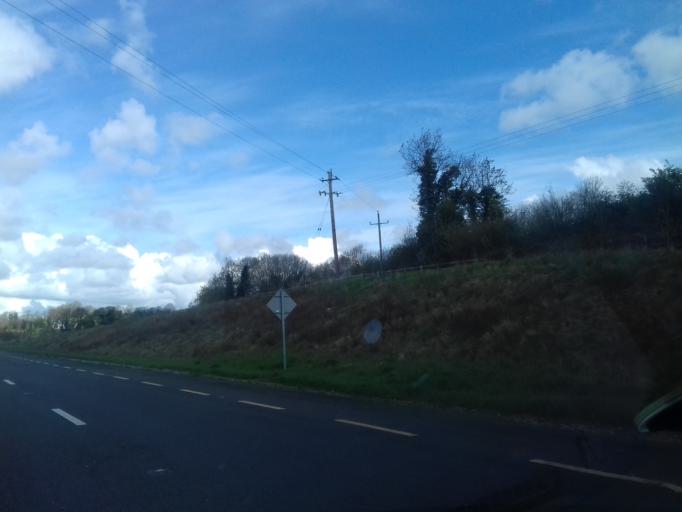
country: IE
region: Ulster
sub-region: An Cabhan
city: Belturbet
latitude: 54.0734
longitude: -7.4147
